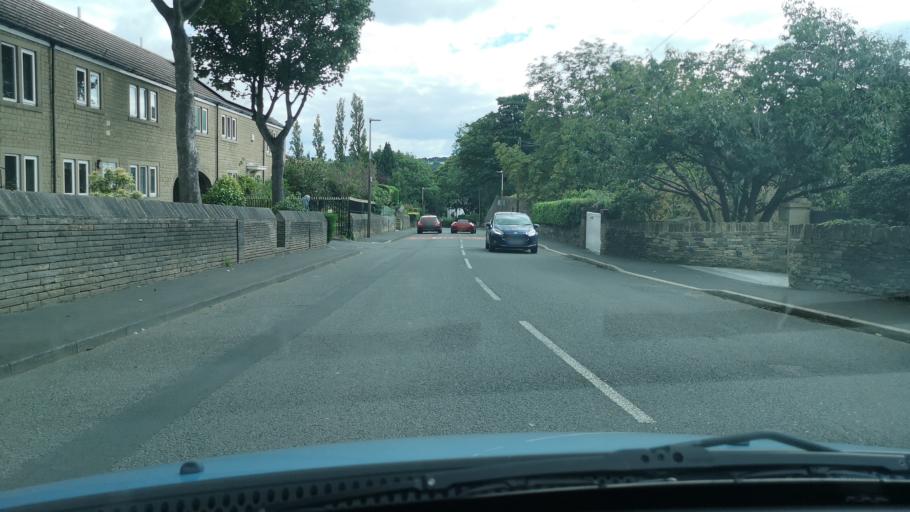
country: GB
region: England
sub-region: Kirklees
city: Mirfield
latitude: 53.6791
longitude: -1.6809
